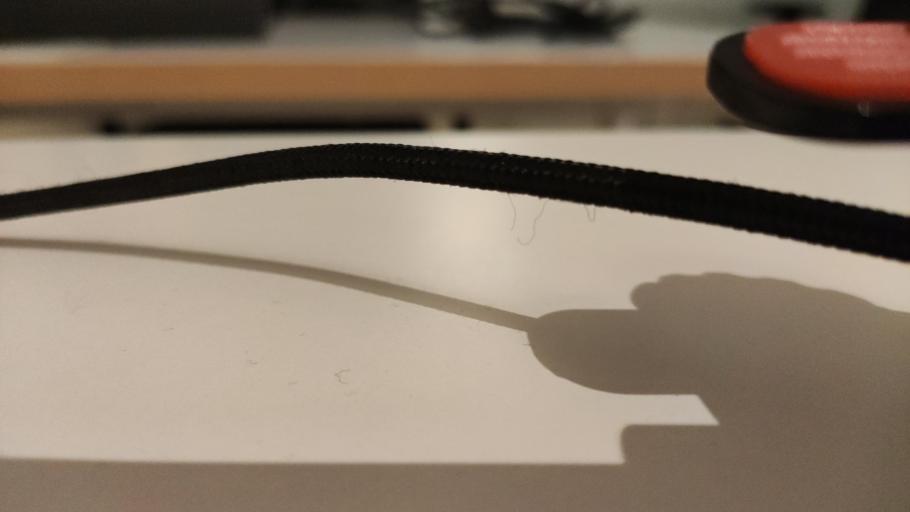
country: RU
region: Moskovskaya
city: Novoye
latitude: 55.6126
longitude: 38.9352
